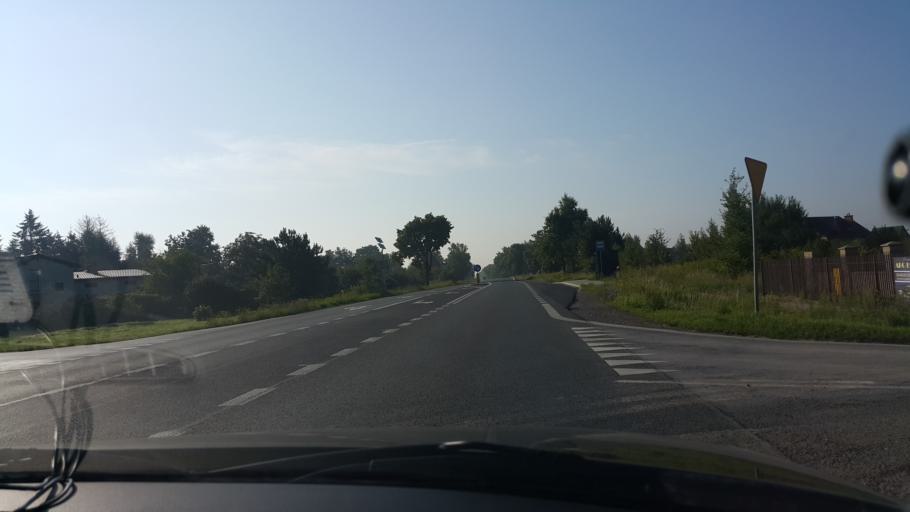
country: PL
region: Masovian Voivodeship
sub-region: Powiat radomski
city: Jedlnia-Letnisko
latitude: 51.4036
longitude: 21.2504
